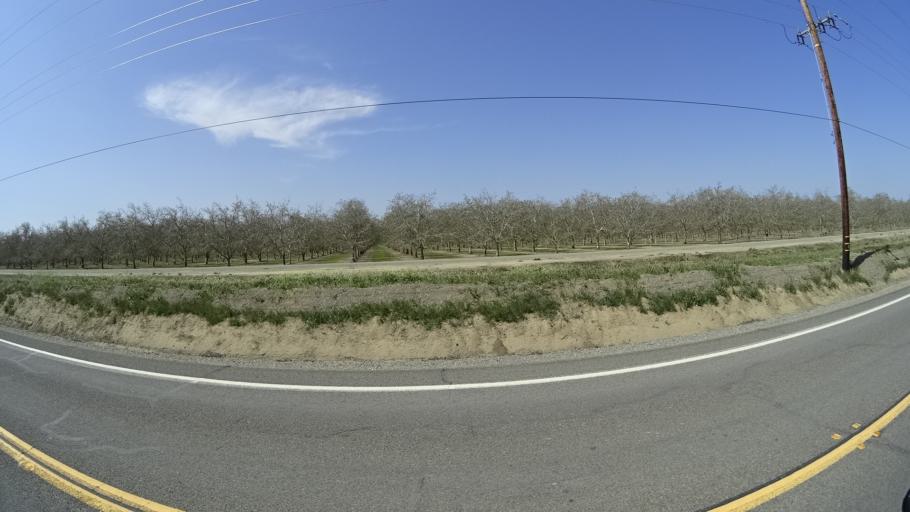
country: US
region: California
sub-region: Glenn County
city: Willows
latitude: 39.5028
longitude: -122.0187
